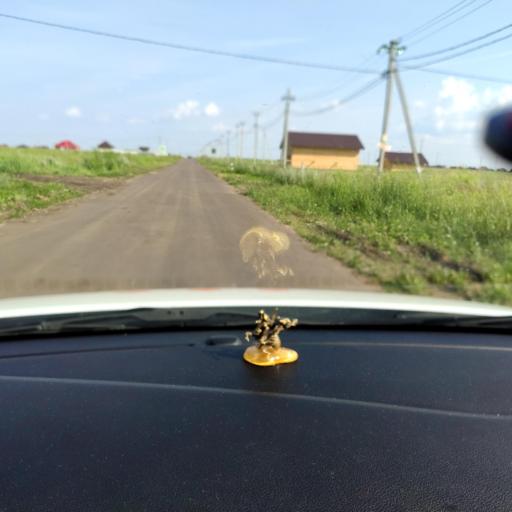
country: RU
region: Tatarstan
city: Laishevo
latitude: 55.4176
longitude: 49.3214
